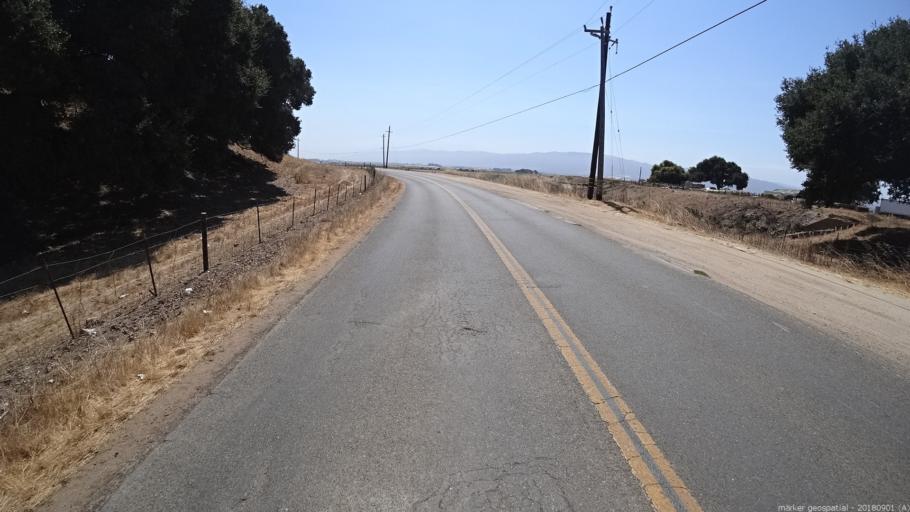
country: US
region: California
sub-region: Monterey County
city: Salinas
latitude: 36.6909
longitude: -121.5688
